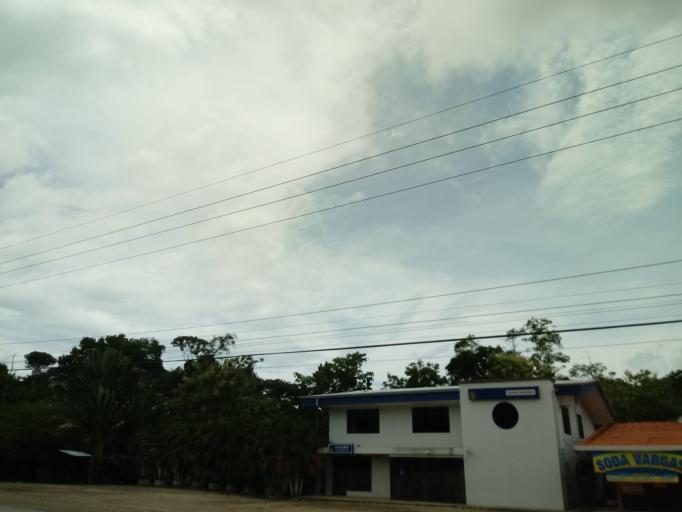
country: CR
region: San Jose
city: Mercedes
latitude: 9.1657
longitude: -83.7359
